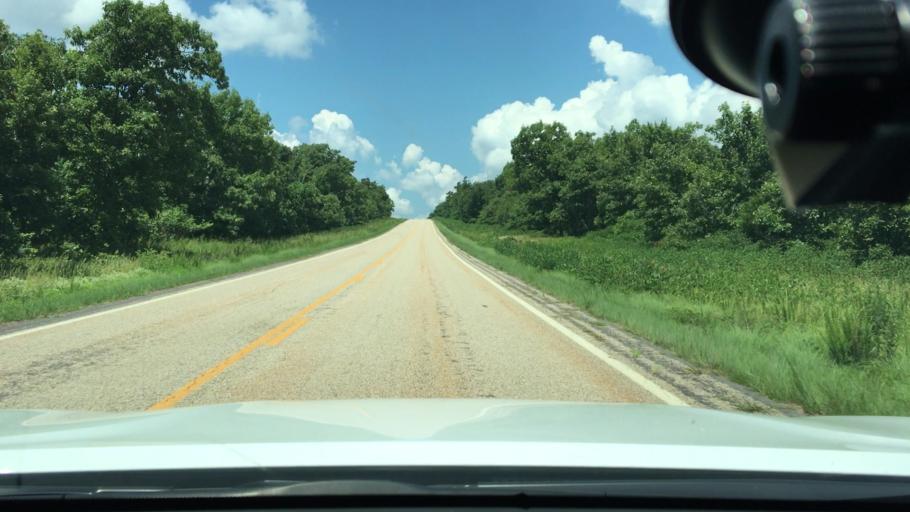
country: US
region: Arkansas
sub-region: Logan County
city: Paris
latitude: 35.1770
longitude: -93.6076
